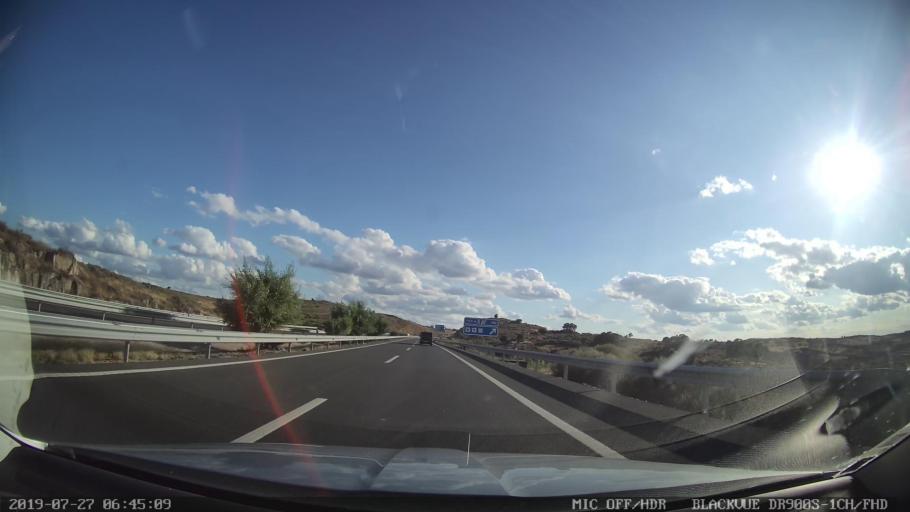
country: ES
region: Extremadura
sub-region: Provincia de Caceres
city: Navalmoral de la Mata
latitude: 39.8830
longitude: -5.5386
